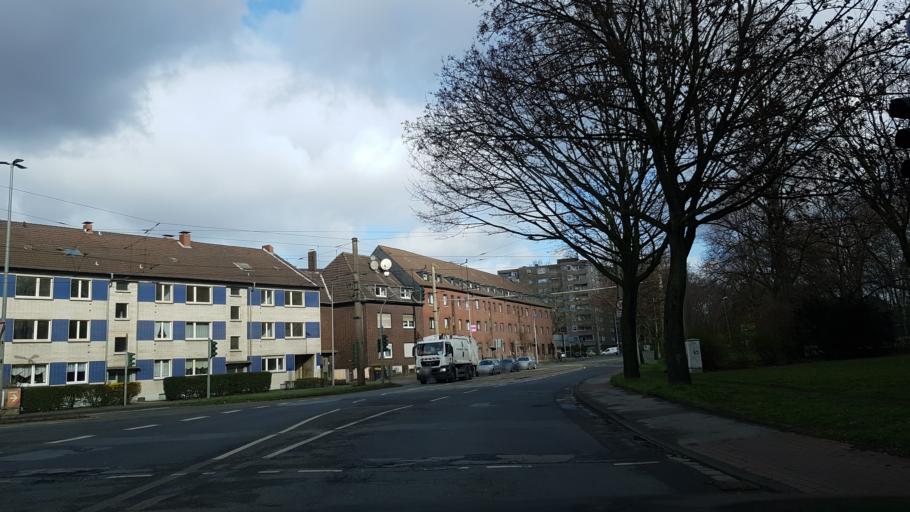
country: DE
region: North Rhine-Westphalia
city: Meiderich
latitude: 51.4734
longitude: 6.7888
